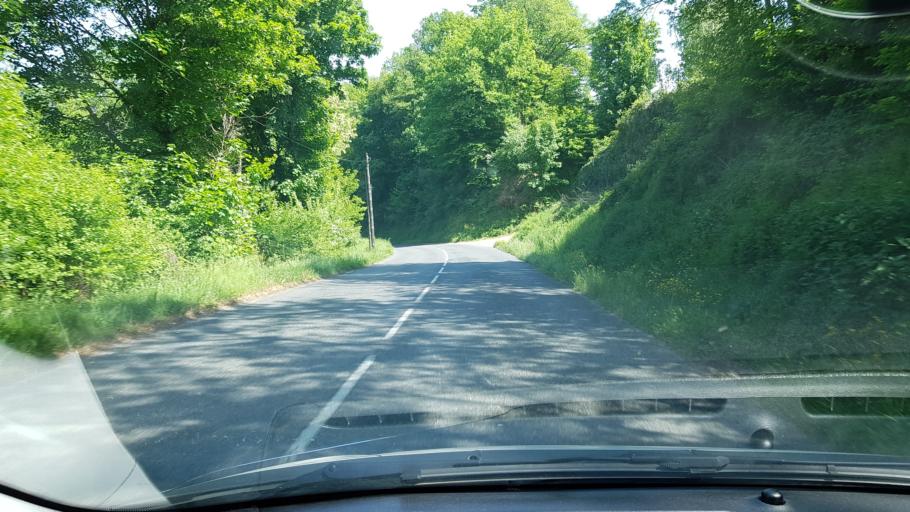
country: FR
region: Rhone-Alpes
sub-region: Departement du Rhone
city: Orlienas
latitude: 45.6603
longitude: 4.7238
